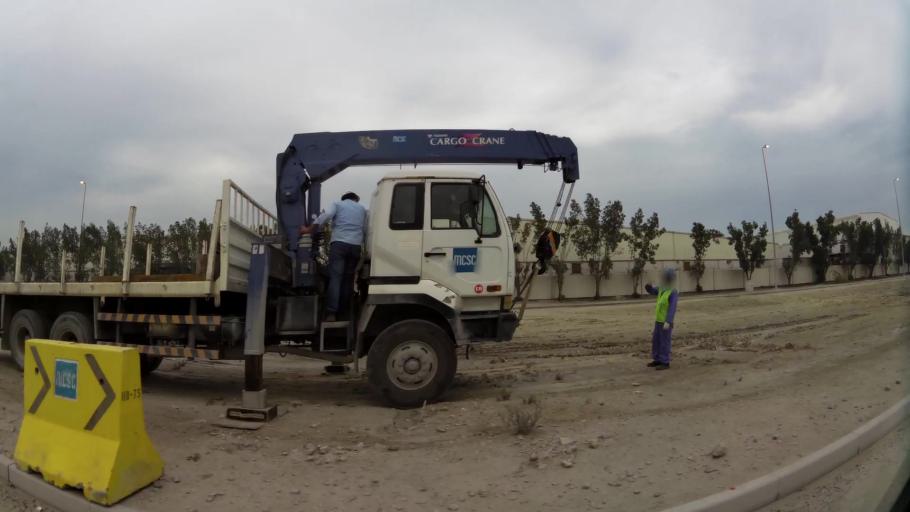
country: BH
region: Northern
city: Sitrah
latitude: 26.1770
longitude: 50.6168
